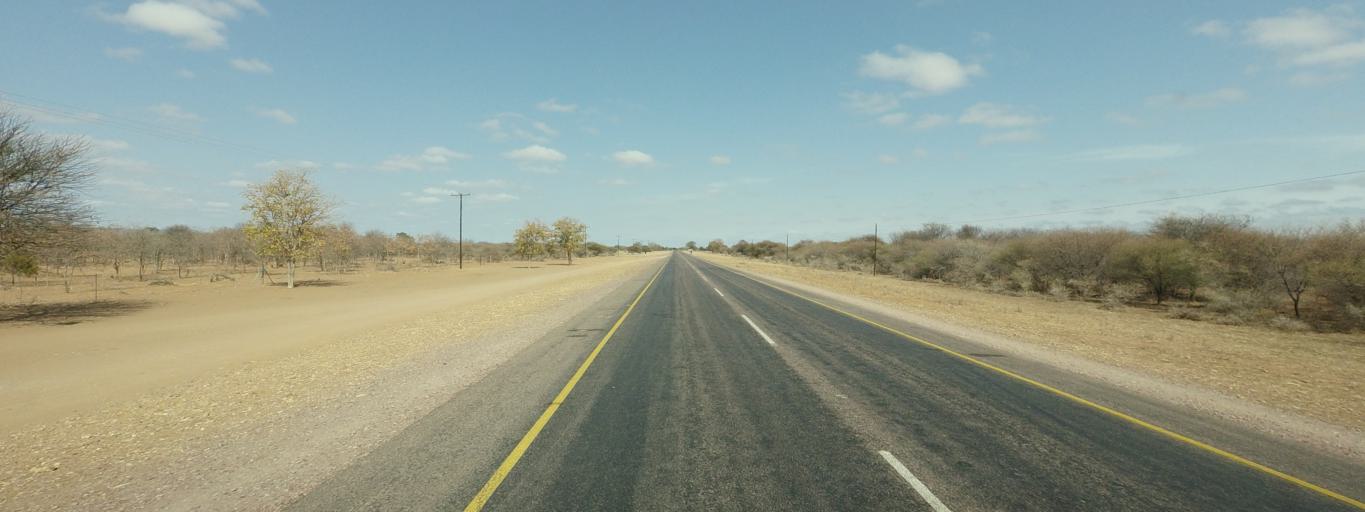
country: BW
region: Central
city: Ramokgonami
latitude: -22.7882
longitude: 27.4364
